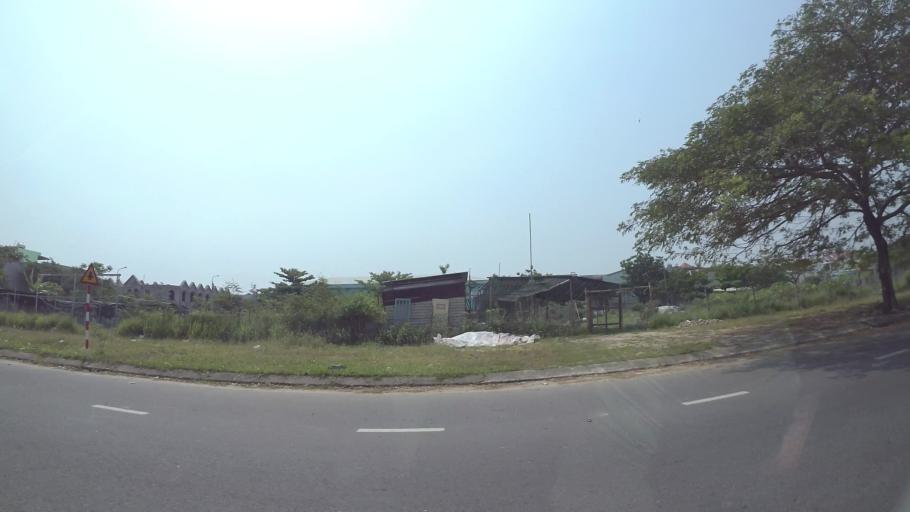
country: VN
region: Da Nang
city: Cam Le
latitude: 15.9945
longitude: 108.2114
